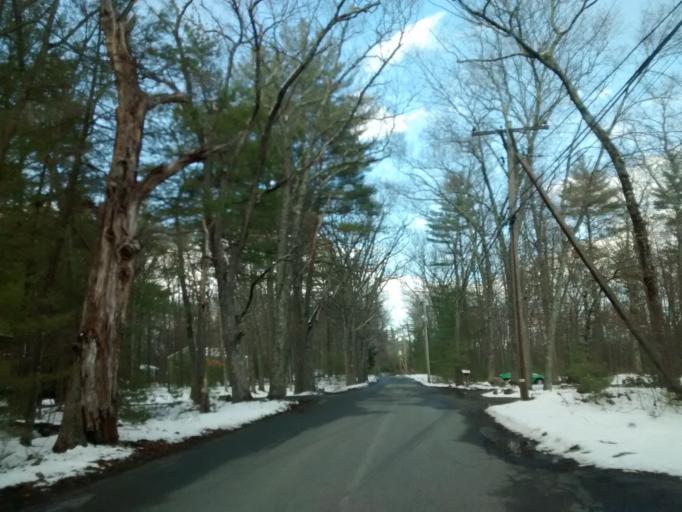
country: US
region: Massachusetts
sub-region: Worcester County
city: Uxbridge
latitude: 42.0306
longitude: -71.6649
